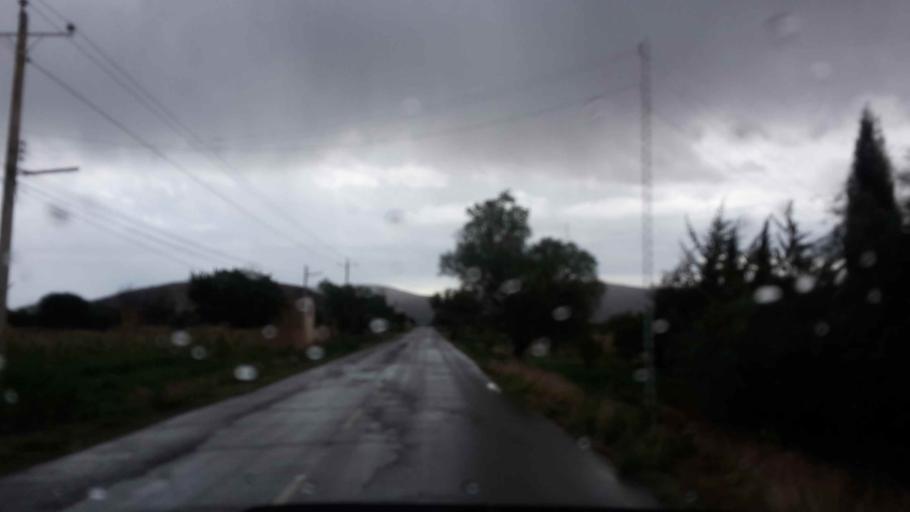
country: BO
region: Cochabamba
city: Tarata
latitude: -17.5591
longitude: -66.0842
